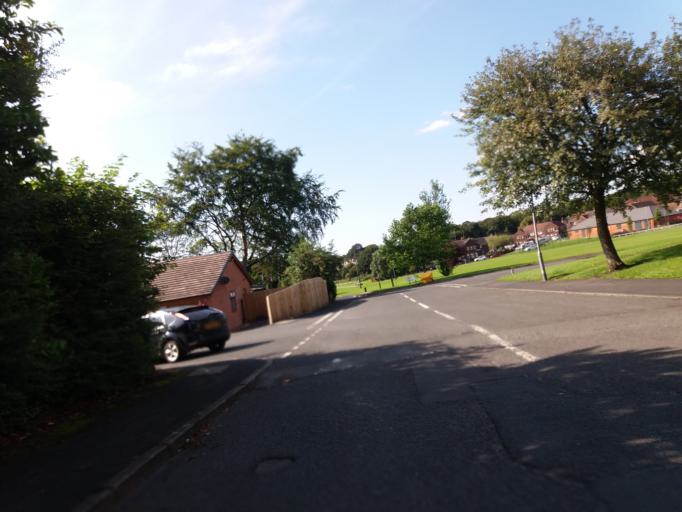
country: GB
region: England
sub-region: Lancashire
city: Coppull
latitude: 53.6419
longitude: -2.6437
